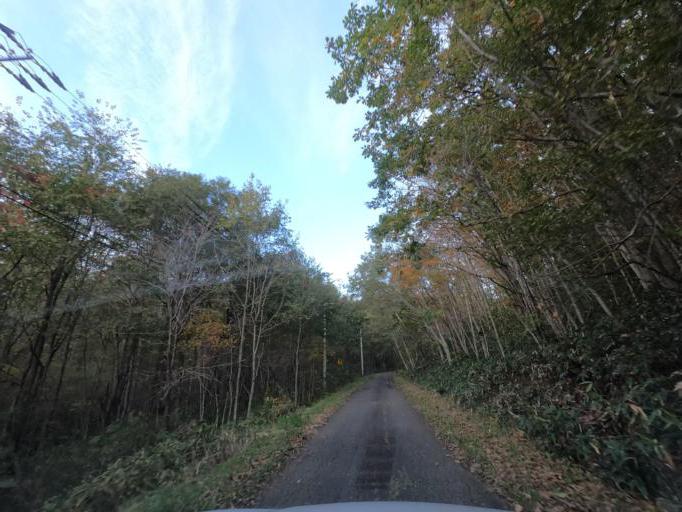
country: JP
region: Hokkaido
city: Obihiro
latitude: 42.5870
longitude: 143.3082
